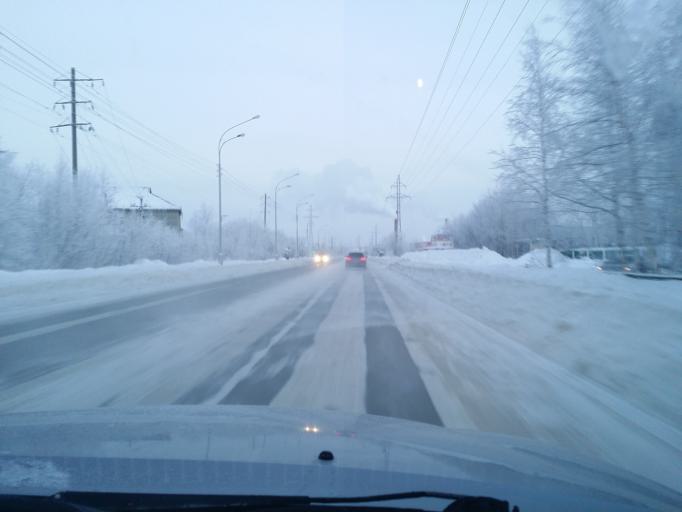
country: RU
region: Khanty-Mansiyskiy Avtonomnyy Okrug
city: Nizhnevartovsk
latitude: 60.9495
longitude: 76.5094
